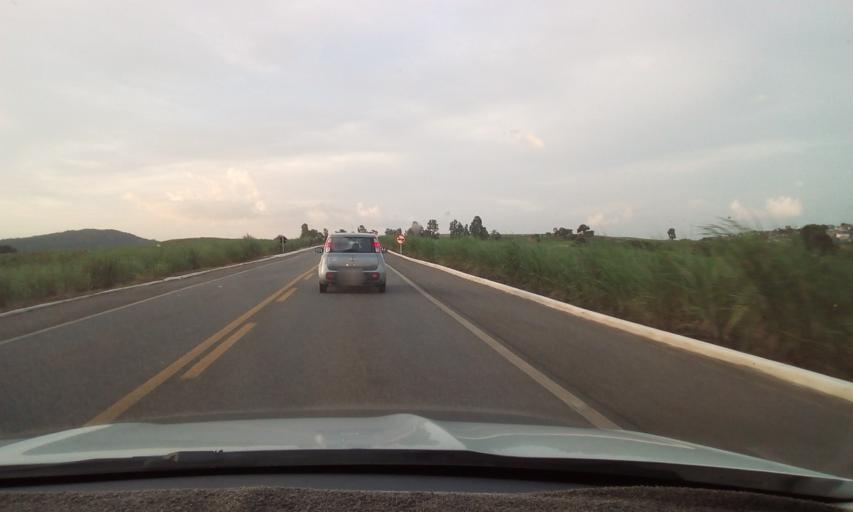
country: BR
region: Pernambuco
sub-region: Vicencia
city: Vicencia
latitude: -7.6069
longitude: -35.2402
